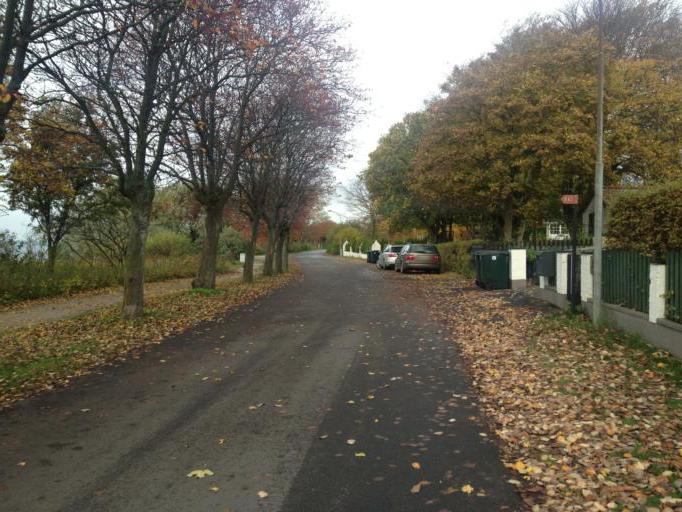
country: SE
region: Skane
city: Bjarred
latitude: 55.7145
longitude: 13.0208
